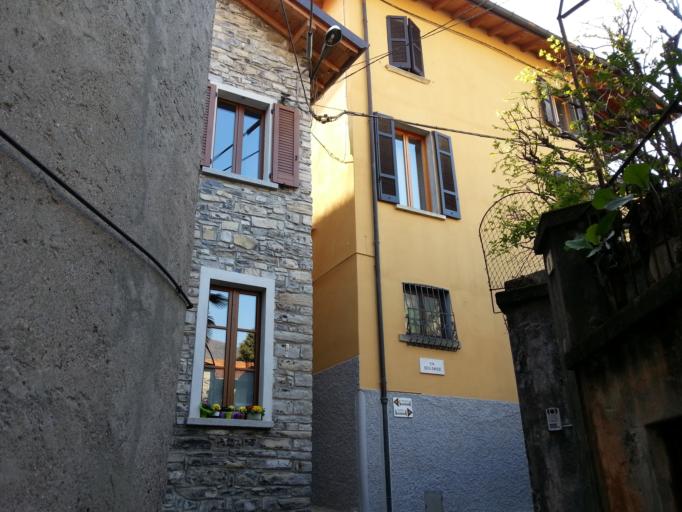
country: IT
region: Lombardy
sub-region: Provincia di Como
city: Torno
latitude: 45.8572
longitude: 9.1171
